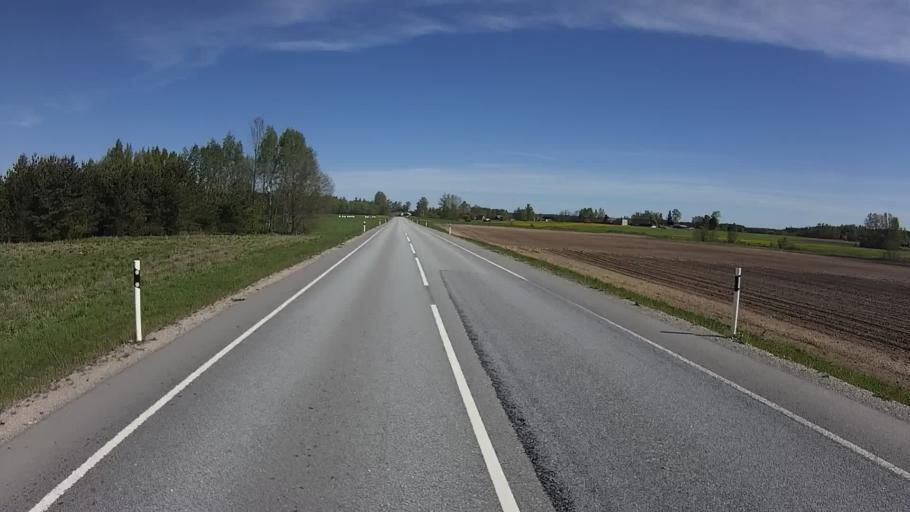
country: RU
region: Pskov
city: Pechory
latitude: 57.9312
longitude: 27.5751
